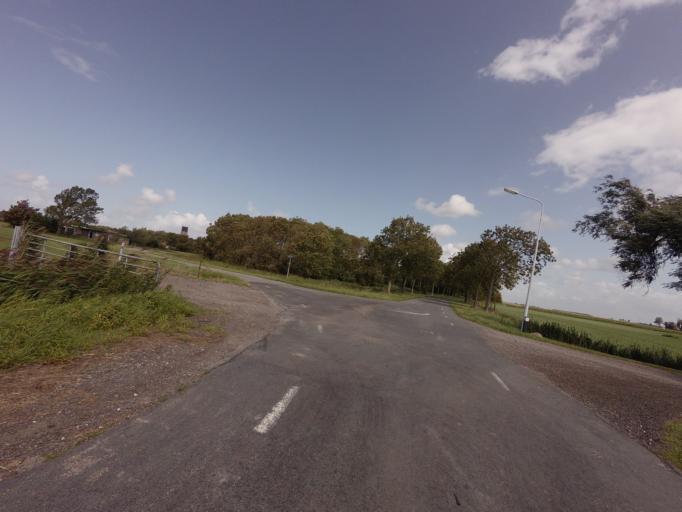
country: NL
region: Friesland
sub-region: Gemeente Harlingen
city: Harlingen
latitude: 53.1119
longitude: 5.4402
